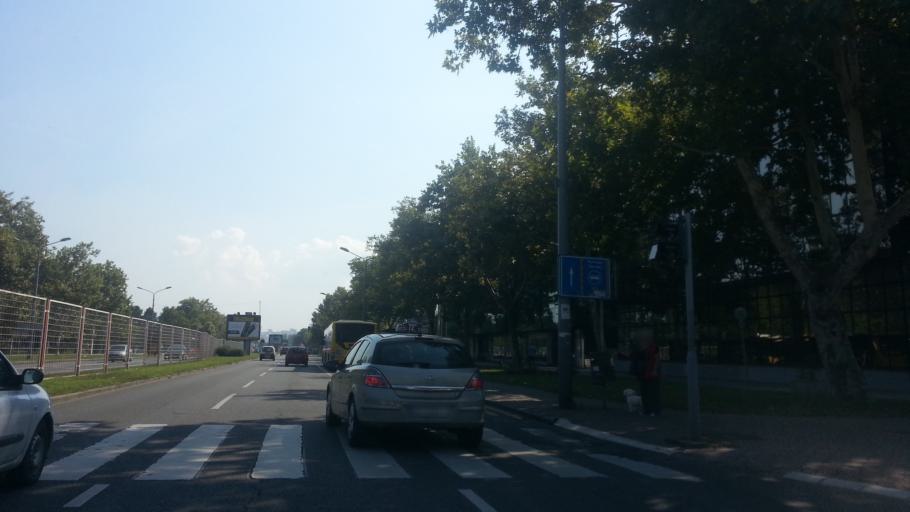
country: RS
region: Central Serbia
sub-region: Belgrade
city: Novi Beograd
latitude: 44.8174
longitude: 20.4281
